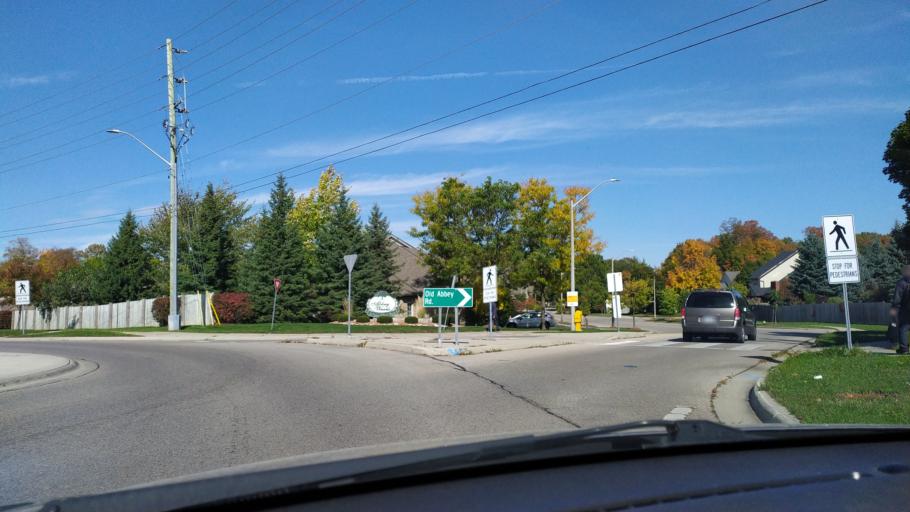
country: CA
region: Ontario
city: Waterloo
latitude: 43.4995
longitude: -80.5253
